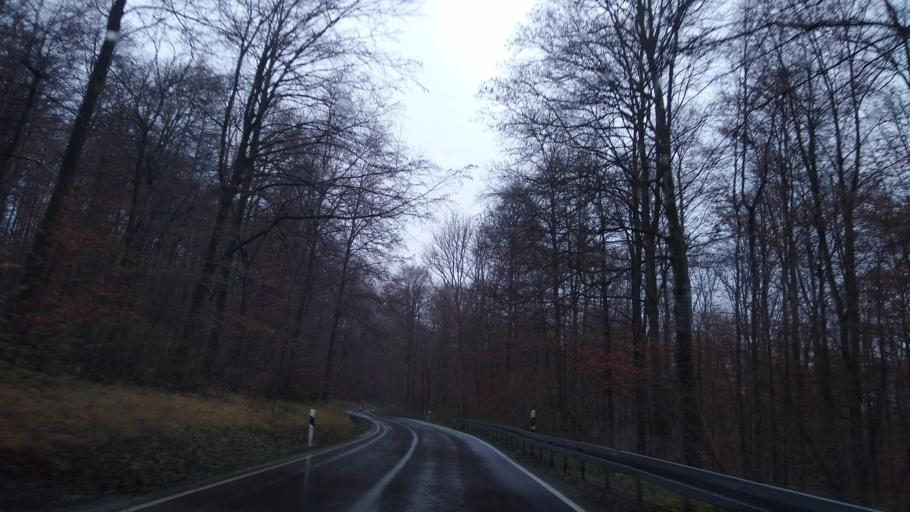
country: DE
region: Lower Saxony
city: Ottenstein
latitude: 51.9666
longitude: 9.4214
